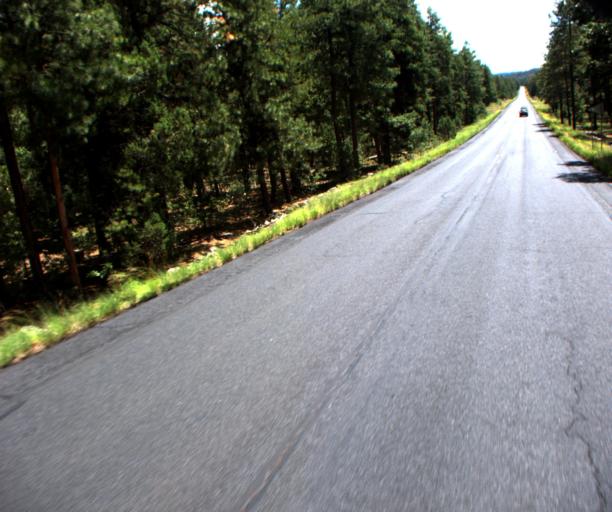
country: US
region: Arizona
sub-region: Gila County
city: Pine
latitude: 34.4839
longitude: -111.4544
